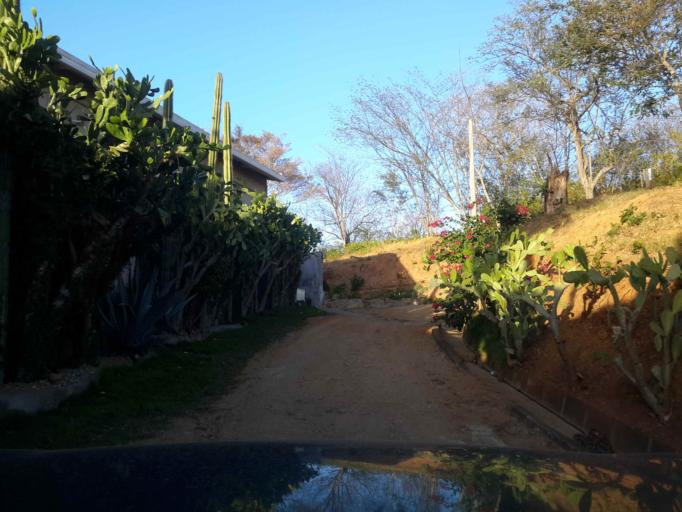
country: NI
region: Rivas
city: San Juan del Sur
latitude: 11.1827
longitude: -85.8125
